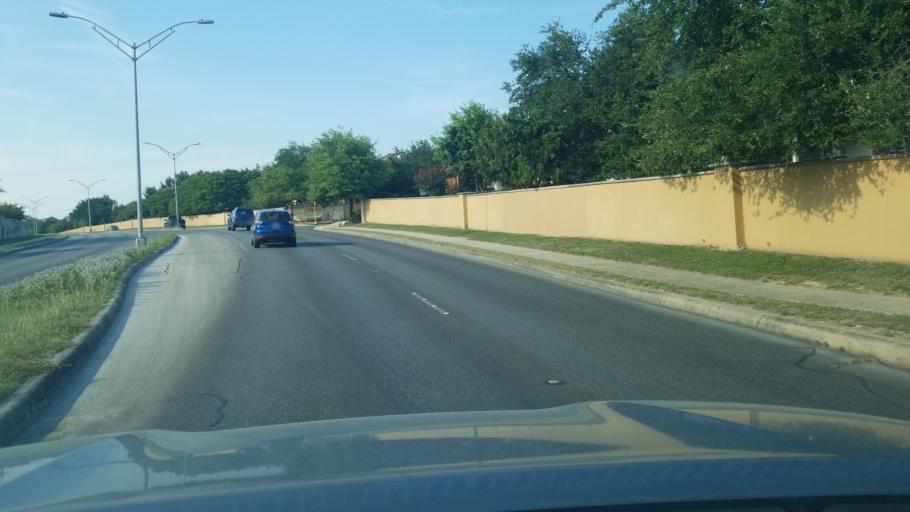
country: US
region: Texas
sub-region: Bexar County
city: Hollywood Park
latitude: 29.6486
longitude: -98.5035
